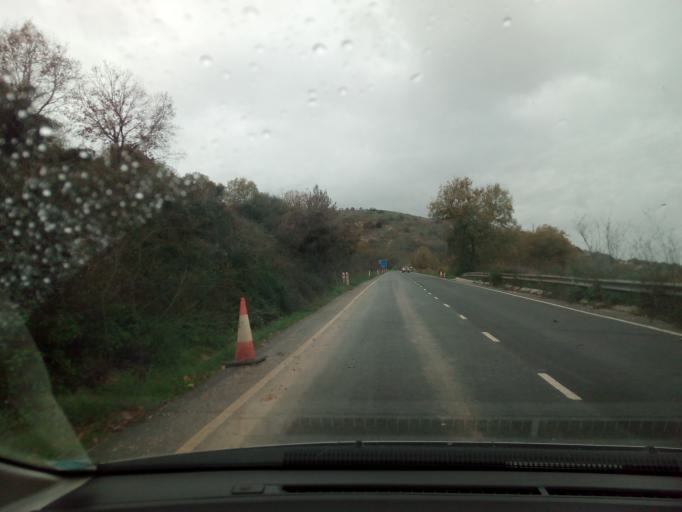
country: CY
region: Pafos
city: Polis
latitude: 34.9604
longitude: 32.4596
